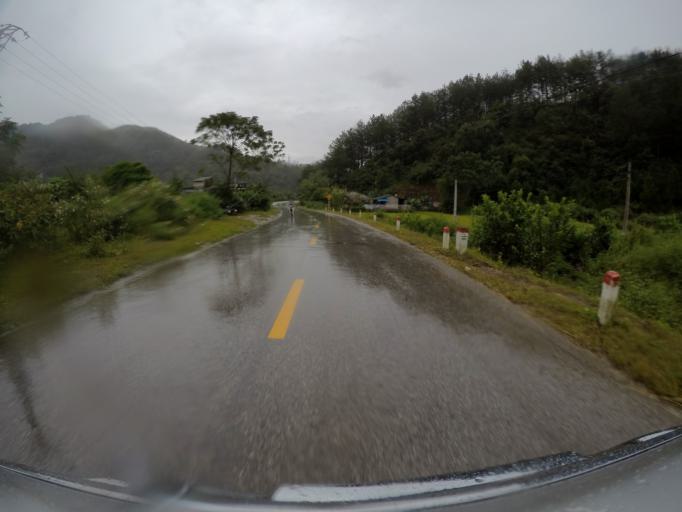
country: VN
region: Lai Chau
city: Than Uyen
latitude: 22.0652
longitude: 103.8727
